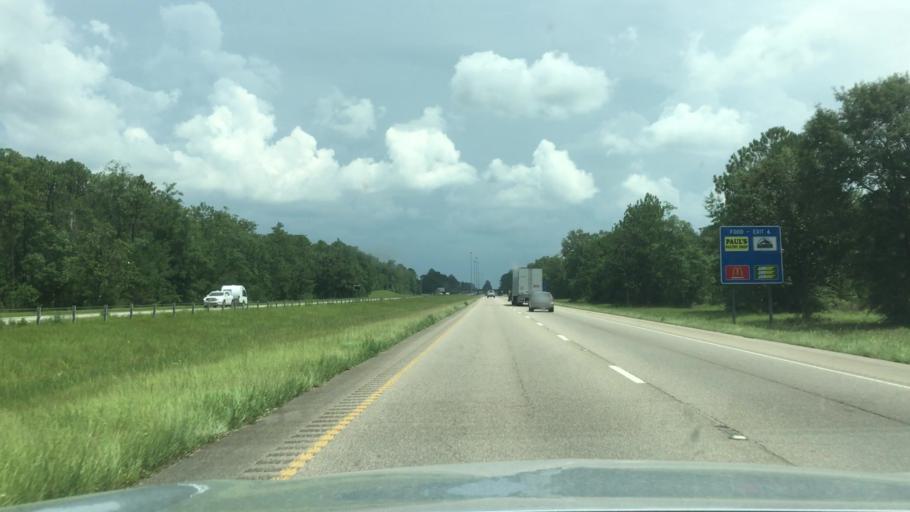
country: US
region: Mississippi
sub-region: Pearl River County
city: Picayune
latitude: 30.5348
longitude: -89.6543
